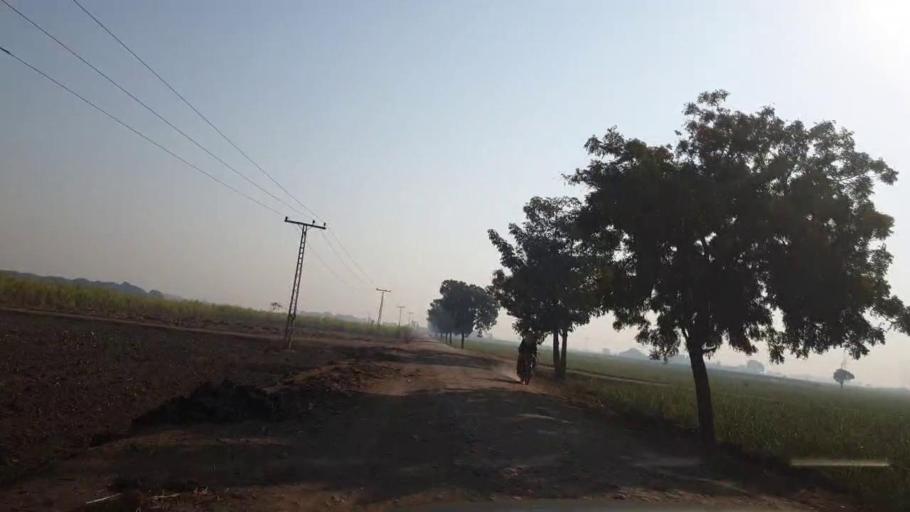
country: PK
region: Sindh
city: Tando Allahyar
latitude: 25.4919
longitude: 68.7234
